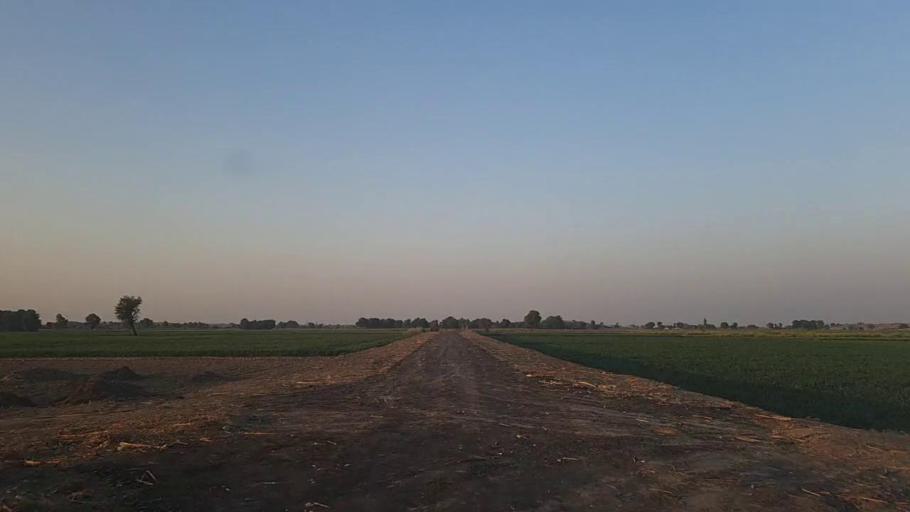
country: PK
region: Sindh
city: Jam Sahib
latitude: 26.3609
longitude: 68.7205
